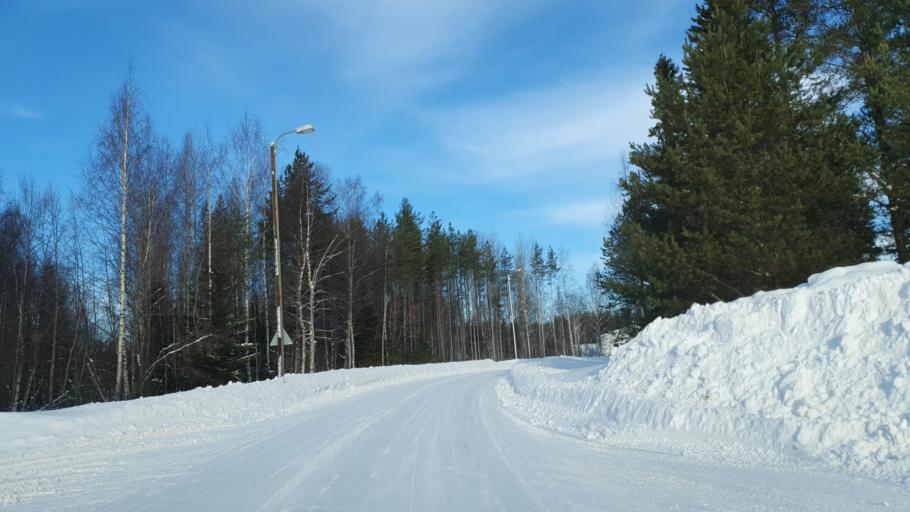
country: FI
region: Northern Ostrobothnia
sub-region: Oulu
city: Haukipudas
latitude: 65.1946
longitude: 25.4108
